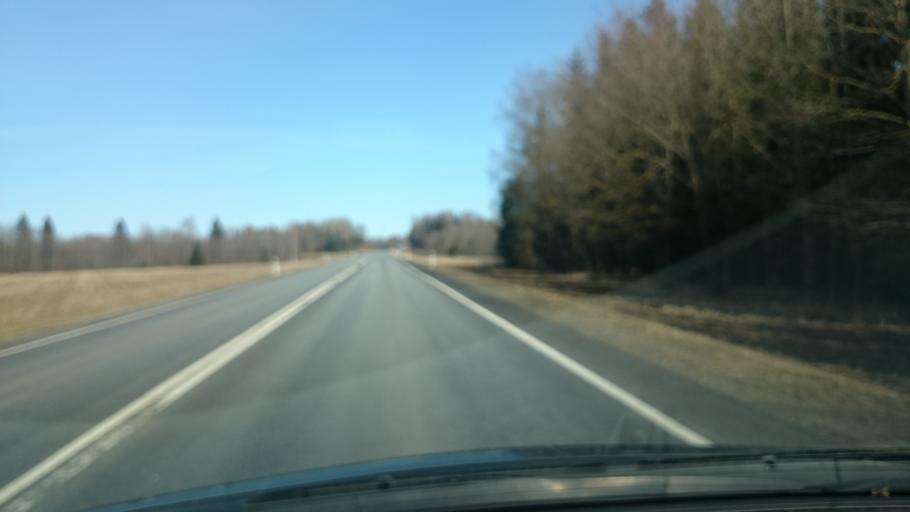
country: EE
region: Paernumaa
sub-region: Vaendra vald (alev)
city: Vandra
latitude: 58.6367
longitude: 24.9601
